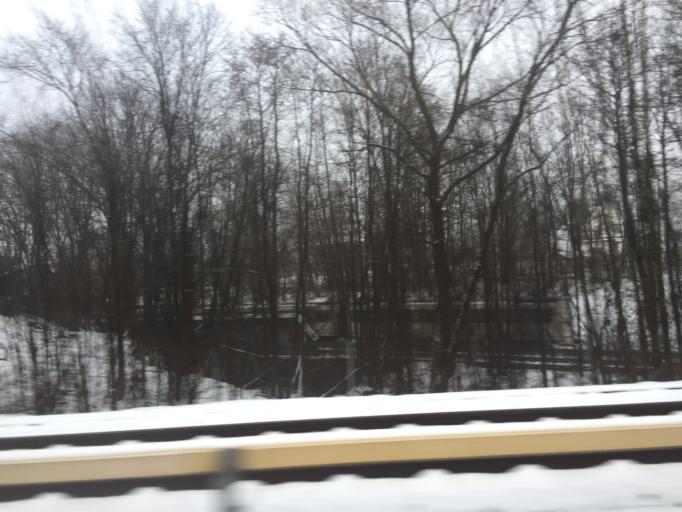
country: NO
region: Oslo
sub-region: Oslo
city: Sjolyststranda
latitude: 59.9356
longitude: 10.7084
